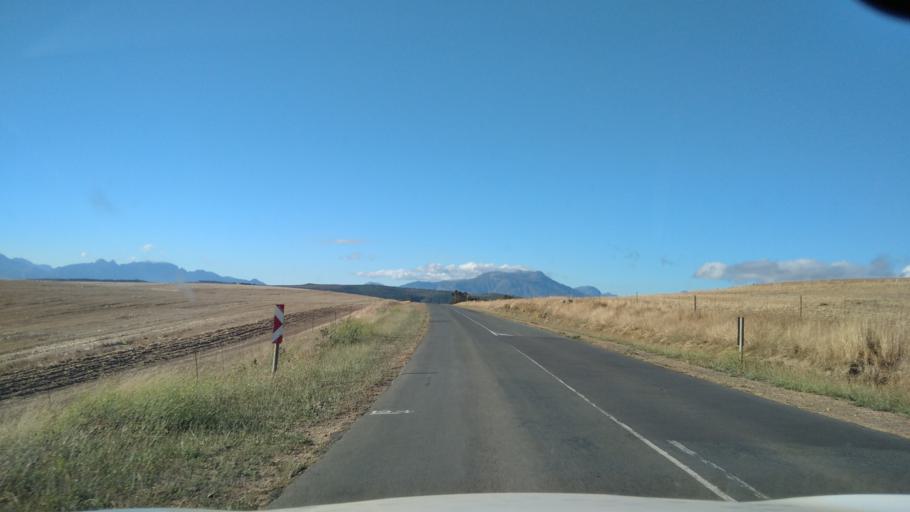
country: ZA
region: Western Cape
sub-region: Overberg District Municipality
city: Caledon
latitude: -34.1472
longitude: 19.2990
